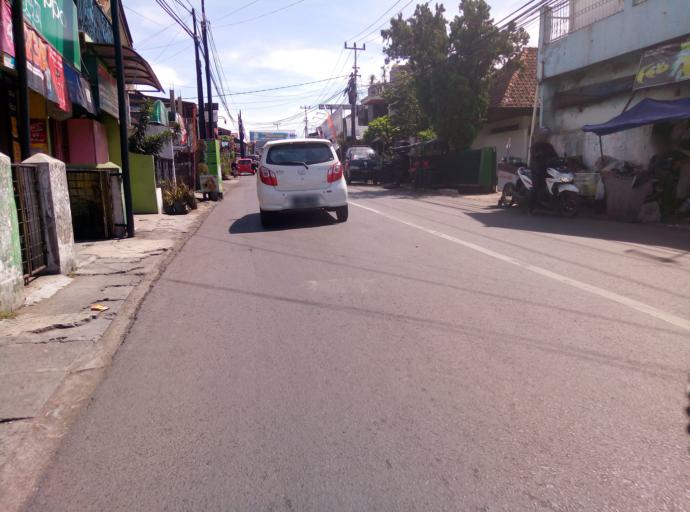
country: ID
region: West Java
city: Bandung
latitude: -6.8922
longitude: 107.6307
